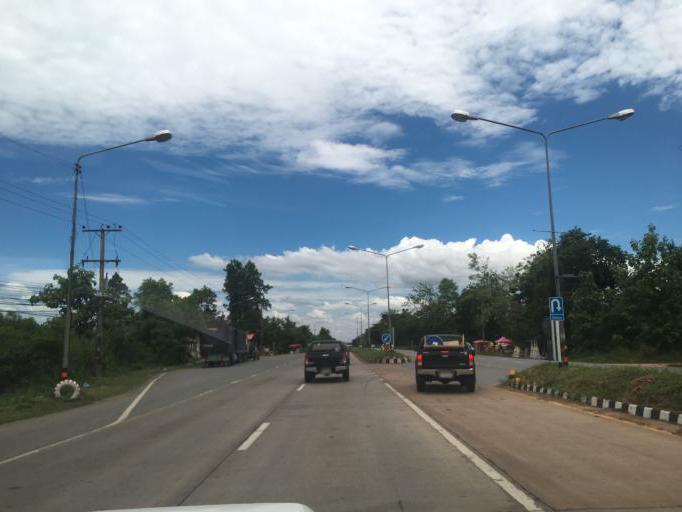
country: TH
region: Khon Kaen
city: Nam Phong
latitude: 16.6405
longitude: 102.7998
